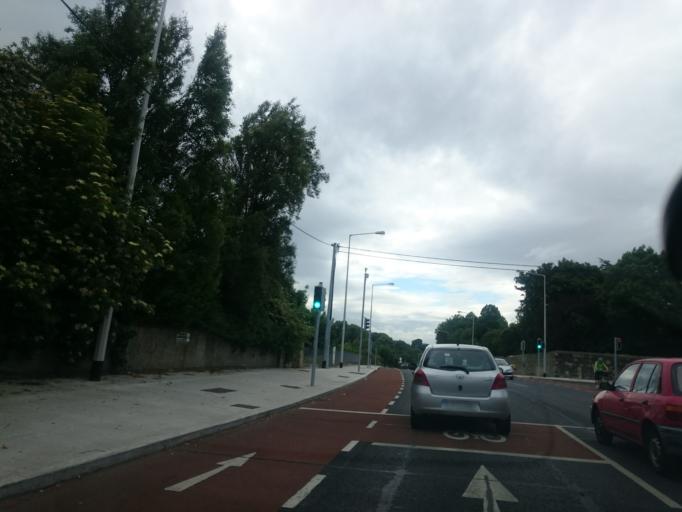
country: IE
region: Leinster
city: Rathgar
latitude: 53.3024
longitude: -6.2668
